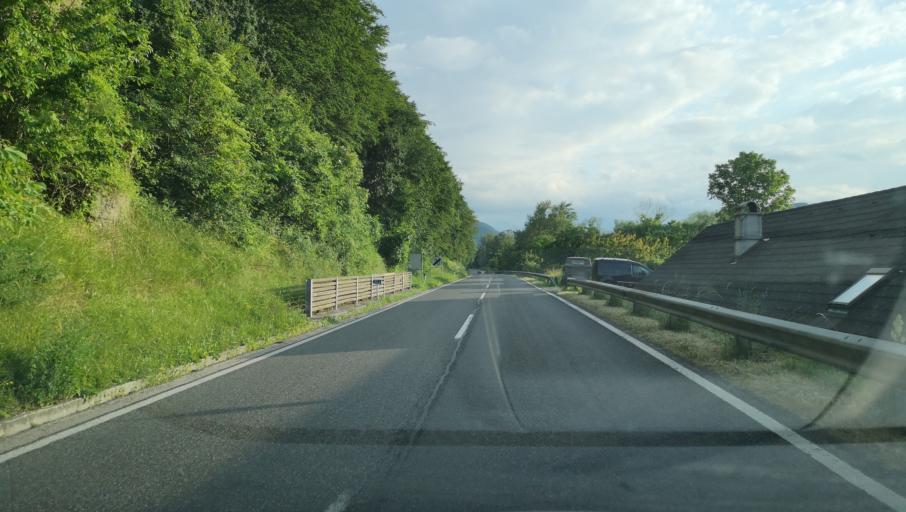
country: AT
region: Lower Austria
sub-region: Politischer Bezirk Krems
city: Durnstein
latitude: 48.3912
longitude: 15.4734
